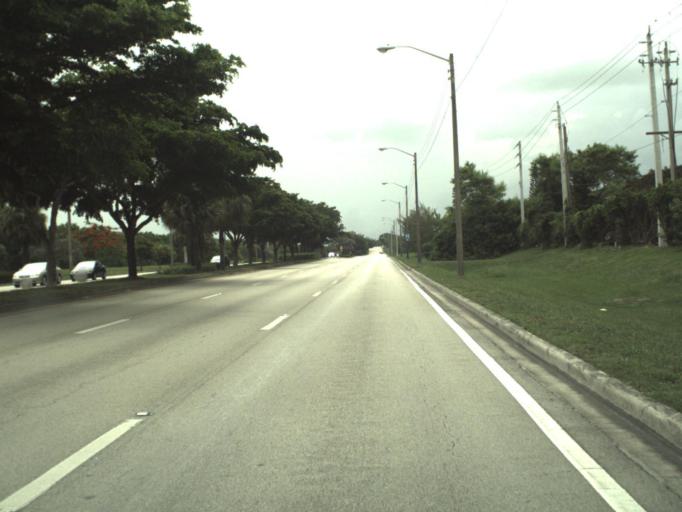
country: US
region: Florida
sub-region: Palm Beach County
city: Boca Del Mar
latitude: 26.3504
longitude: -80.1609
